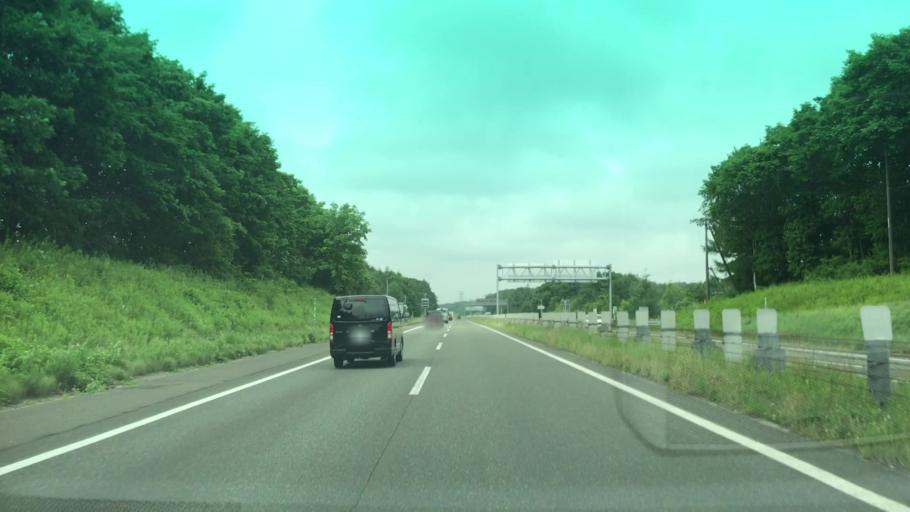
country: JP
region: Hokkaido
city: Tomakomai
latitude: 42.7174
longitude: 141.6525
